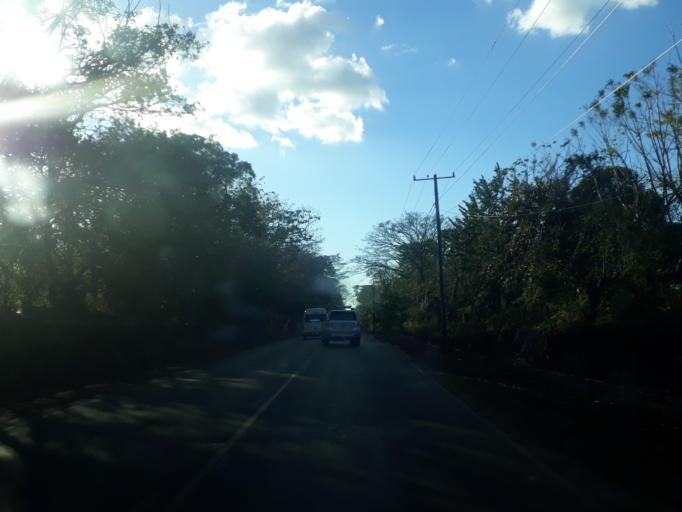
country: NI
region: Carazo
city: La Paz de Oriente
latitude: 11.8089
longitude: -86.1192
